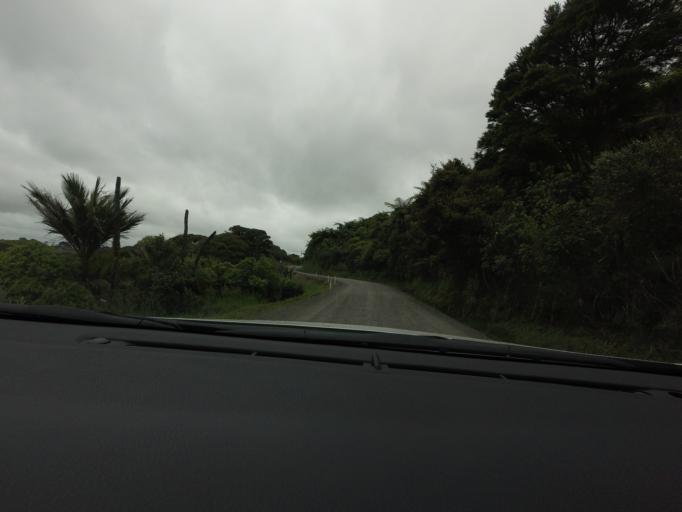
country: NZ
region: Auckland
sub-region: Auckland
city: Warkworth
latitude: -36.4831
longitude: 174.6025
